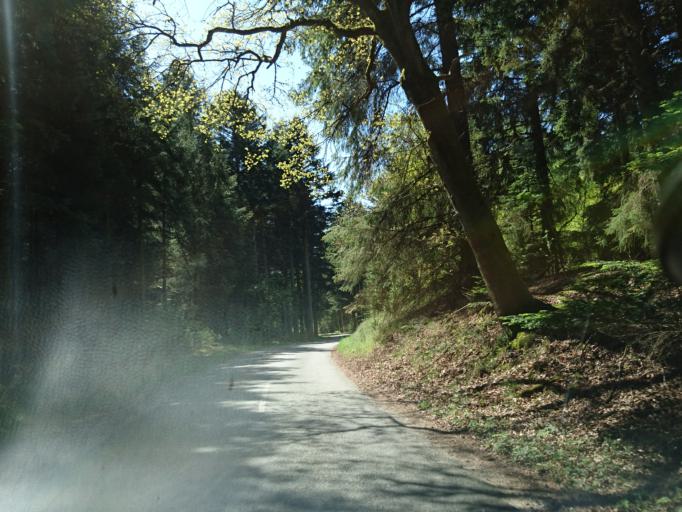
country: DK
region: North Denmark
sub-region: Hjorring Kommune
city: Sindal
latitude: 57.5988
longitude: 10.2319
